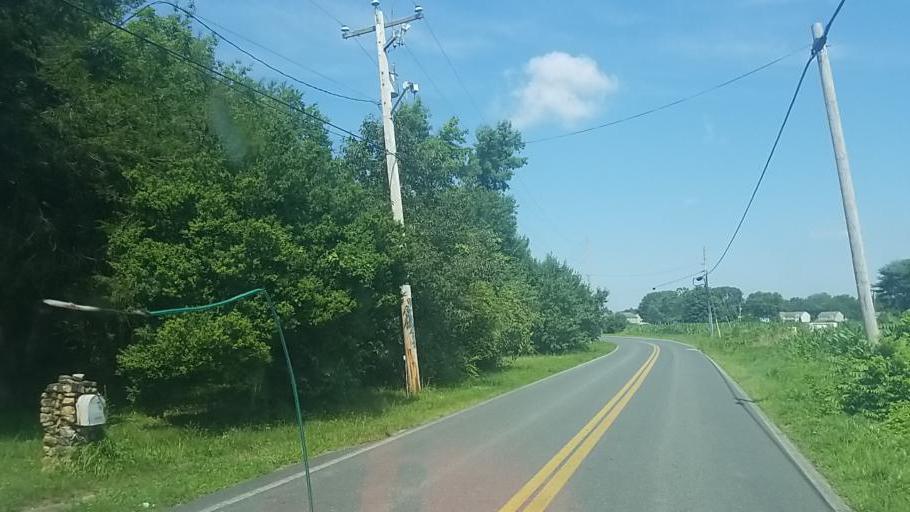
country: US
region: Maryland
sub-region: Caroline County
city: Denton
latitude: 38.8830
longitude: -75.7987
